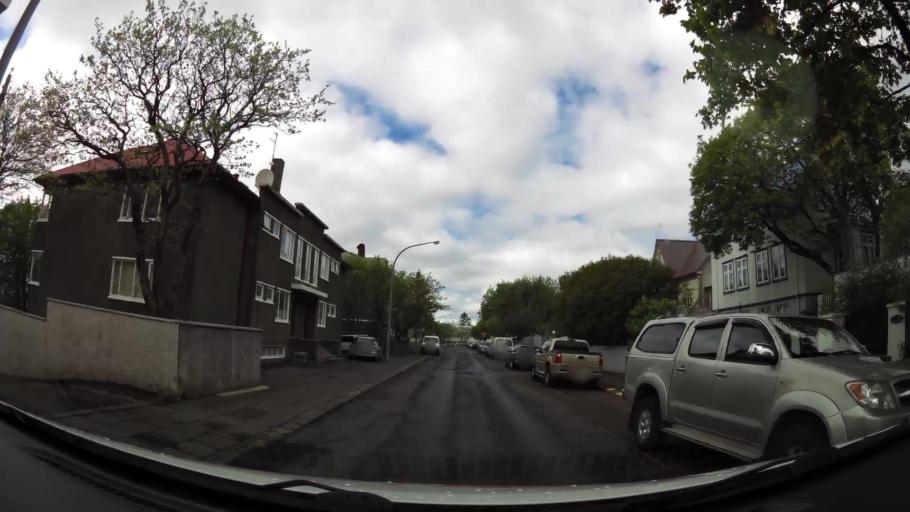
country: IS
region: Capital Region
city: Kopavogur
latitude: 64.1401
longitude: -21.9346
